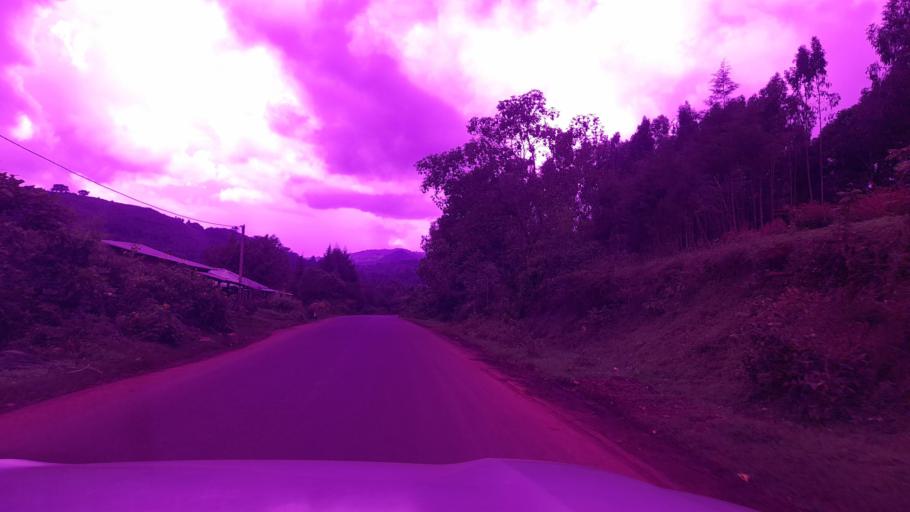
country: ET
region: Oromiya
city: Jima
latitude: 7.6712
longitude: 36.8929
